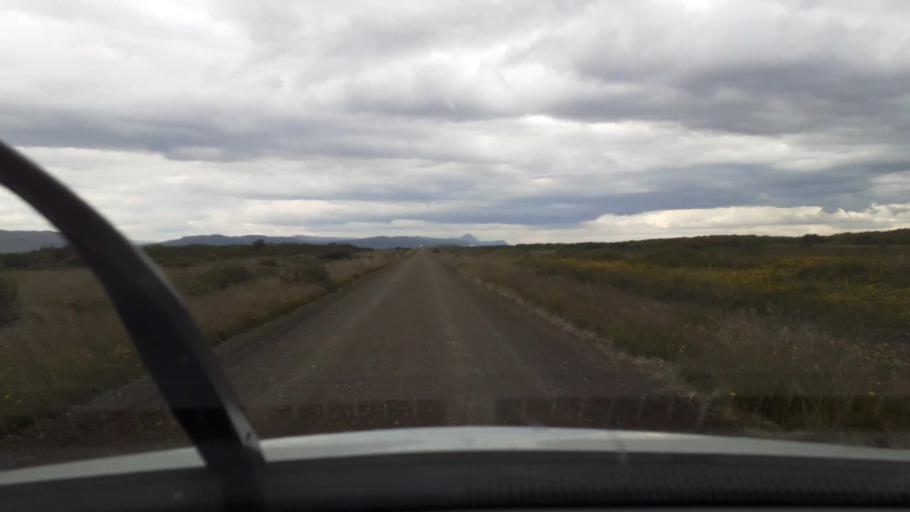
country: IS
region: West
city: Borgarnes
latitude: 64.6371
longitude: -21.9089
